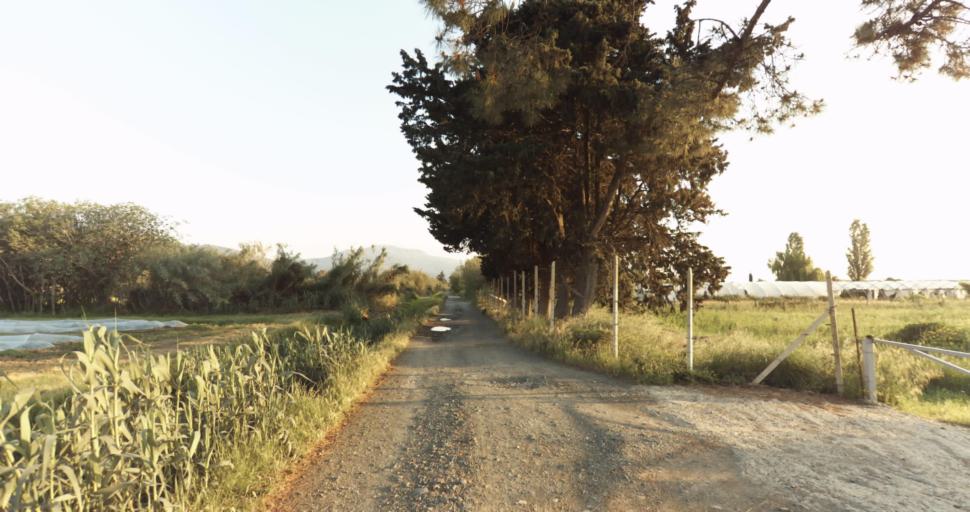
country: FR
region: Corsica
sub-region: Departement de la Haute-Corse
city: Biguglia
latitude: 42.6120
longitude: 9.4468
